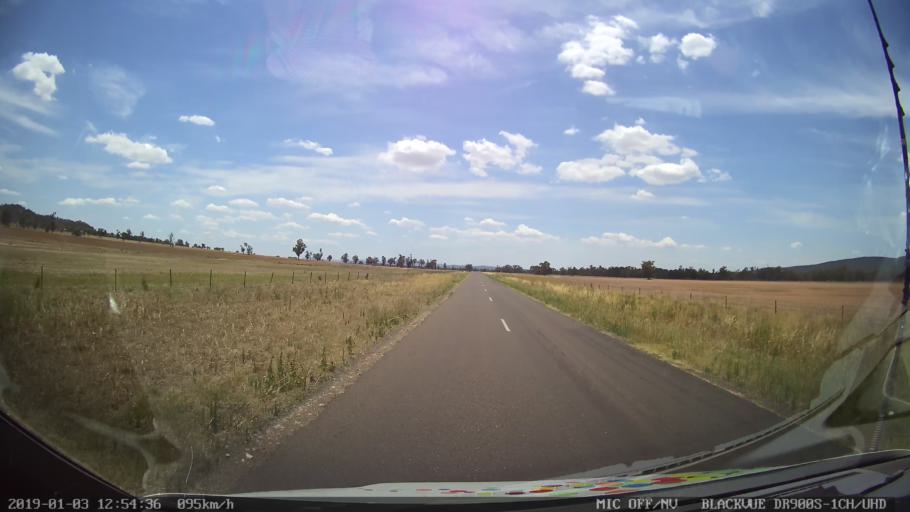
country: AU
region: New South Wales
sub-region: Weddin
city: Grenfell
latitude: -33.6511
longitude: 148.3191
